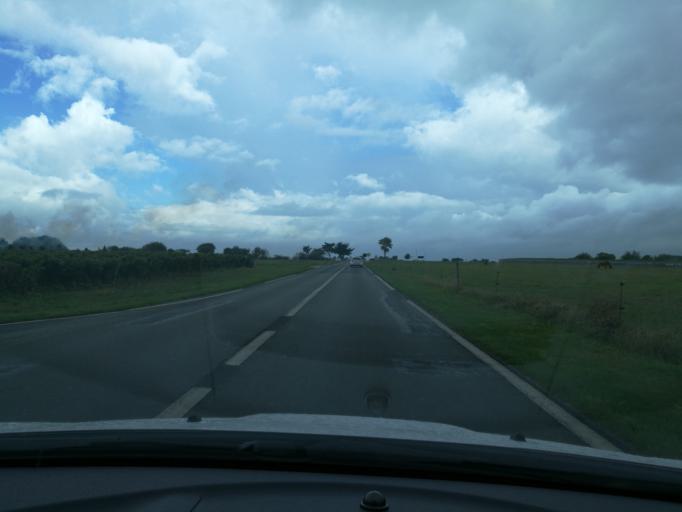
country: FR
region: Poitou-Charentes
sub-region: Departement de la Charente-Maritime
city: Saint-Martin-de-Re
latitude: 46.1992
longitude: -1.3726
